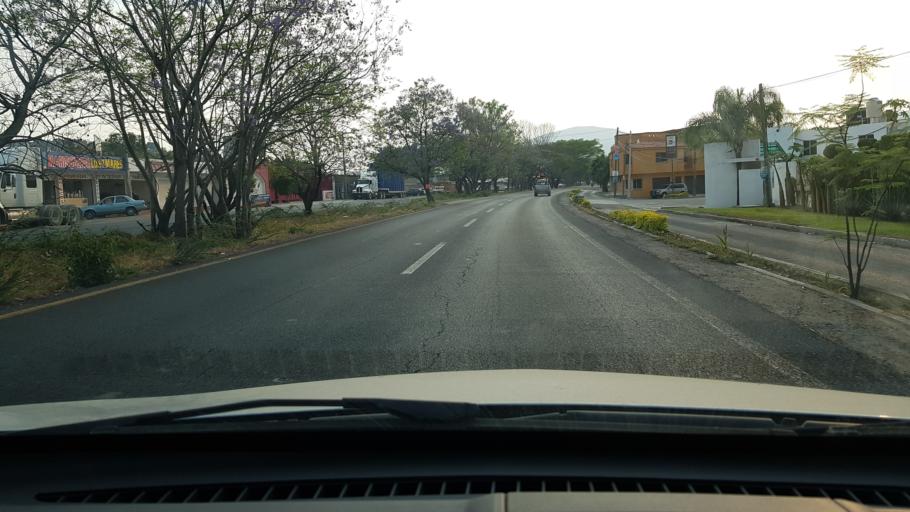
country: MX
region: Morelos
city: Yautepec
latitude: 18.8710
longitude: -99.0614
